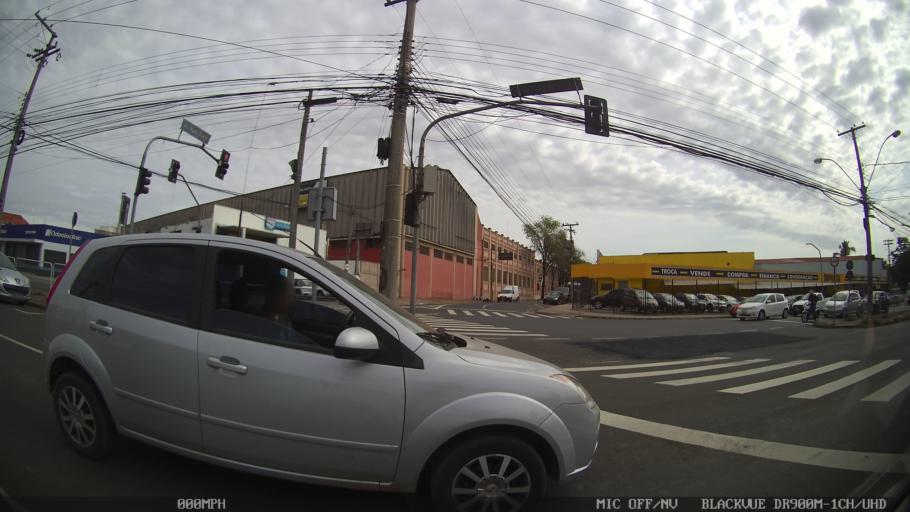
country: BR
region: Sao Paulo
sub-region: Piracicaba
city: Piracicaba
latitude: -22.7074
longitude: -47.6539
